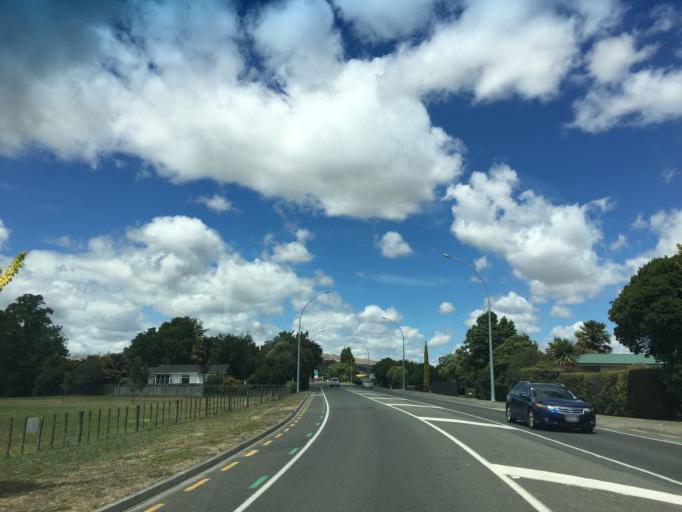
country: NZ
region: Hawke's Bay
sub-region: Hastings District
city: Hastings
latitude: -39.6598
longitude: 176.8852
